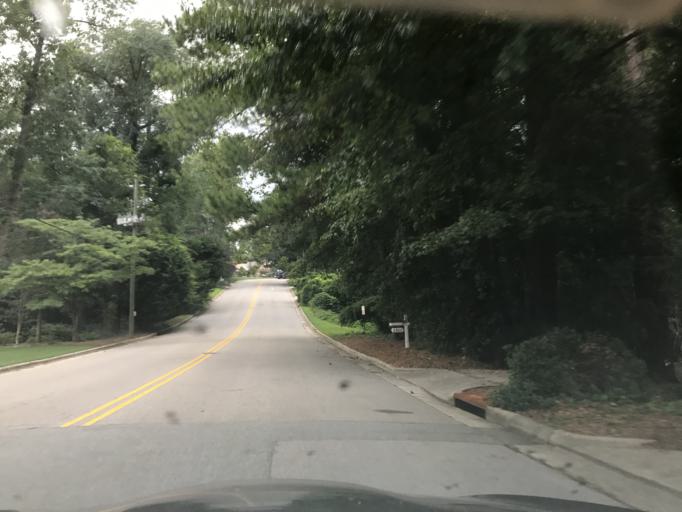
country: US
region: North Carolina
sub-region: Wake County
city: West Raleigh
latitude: 35.8101
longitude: -78.6634
